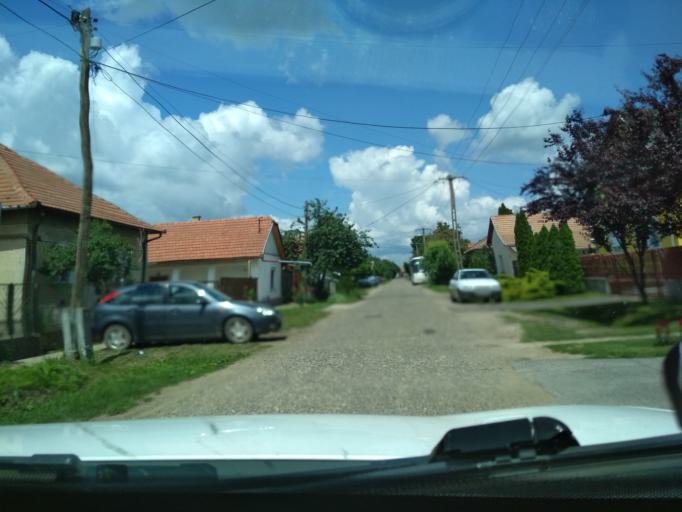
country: HU
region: Jasz-Nagykun-Szolnok
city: Tiszafured
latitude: 47.6102
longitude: 20.7739
